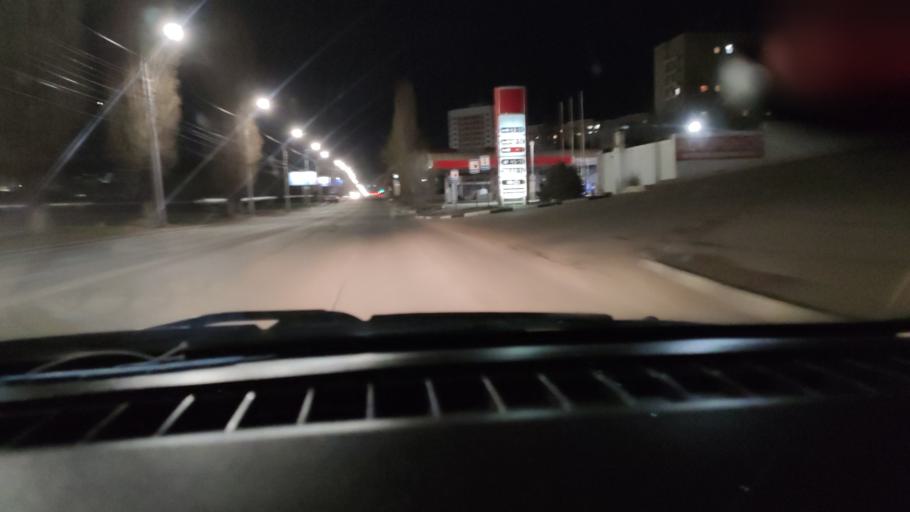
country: RU
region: Saratov
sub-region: Saratovskiy Rayon
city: Saratov
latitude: 51.5695
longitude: 45.9960
